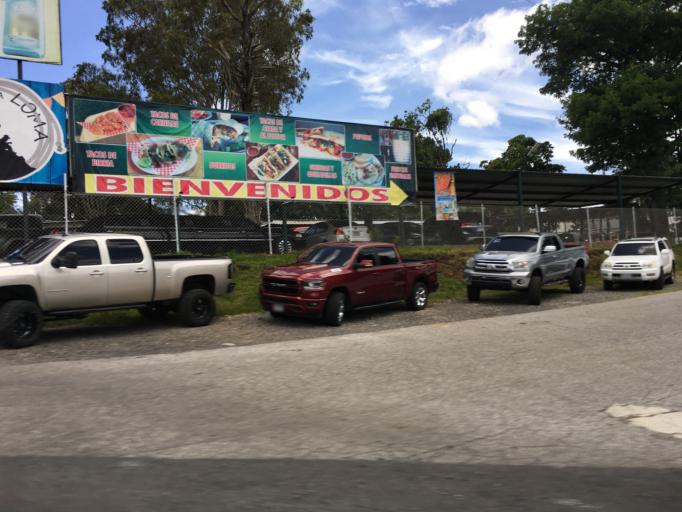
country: GT
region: Guatemala
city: Mixco
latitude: 14.5953
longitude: -90.5682
